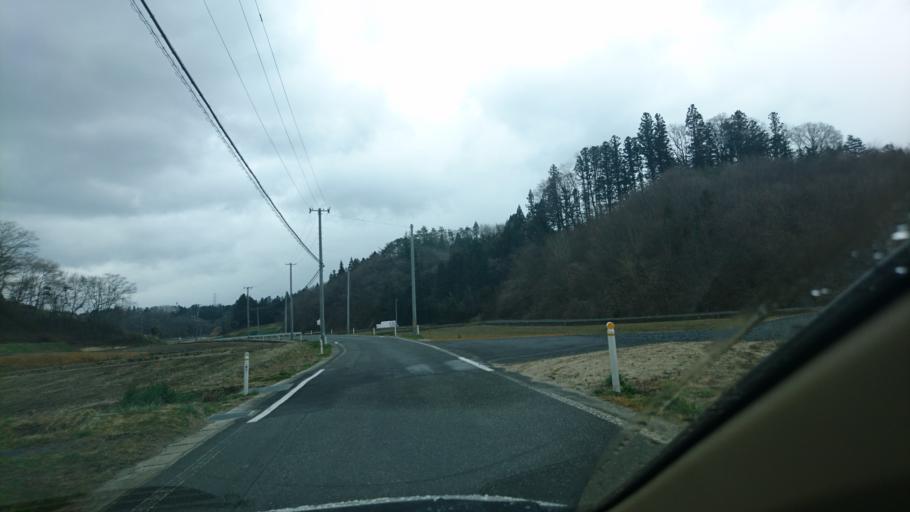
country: JP
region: Iwate
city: Ichinoseki
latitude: 38.9546
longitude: 141.3250
